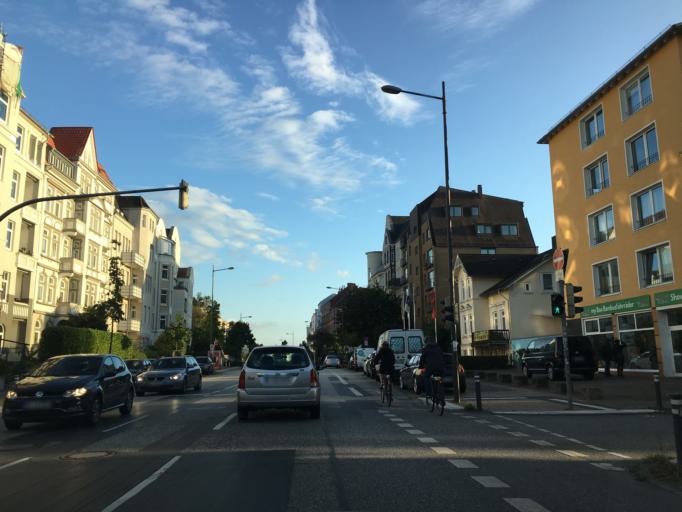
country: DE
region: Schleswig-Holstein
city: Kiel
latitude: 54.3426
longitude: 10.1333
